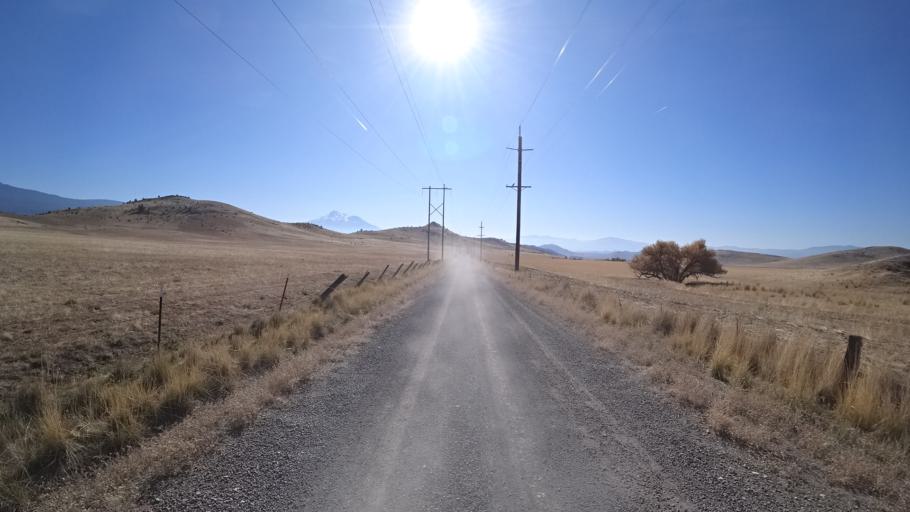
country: US
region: California
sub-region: Siskiyou County
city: Montague
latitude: 41.7551
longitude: -122.3593
